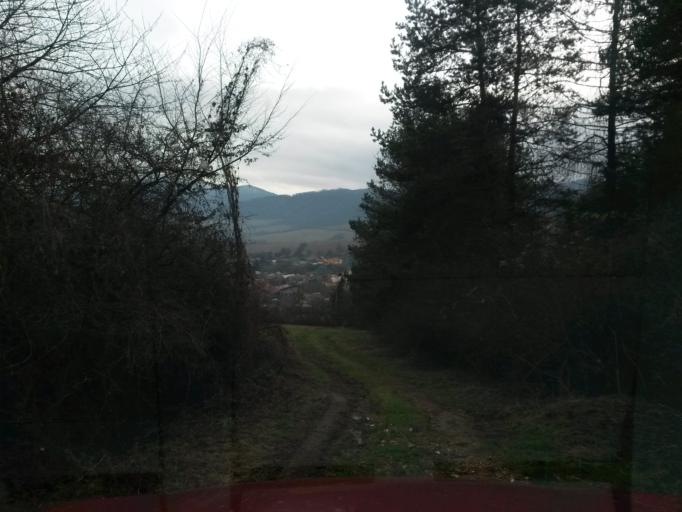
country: SK
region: Kosicky
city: Dobsina
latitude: 48.7282
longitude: 20.4107
